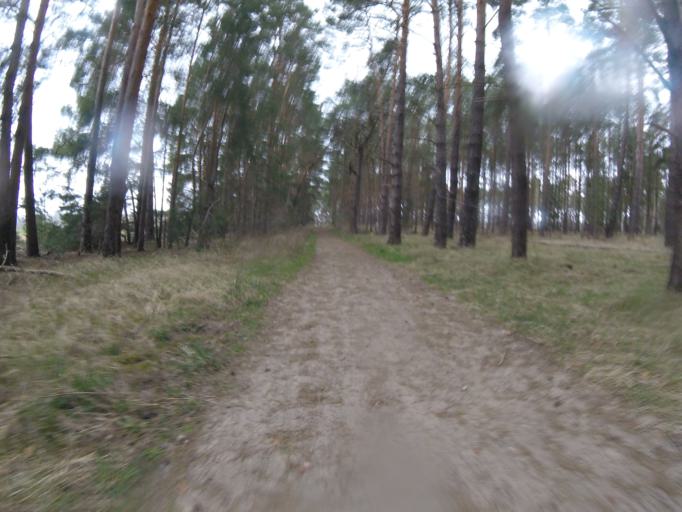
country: DE
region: Brandenburg
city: Schwerin
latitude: 52.1997
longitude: 13.5917
